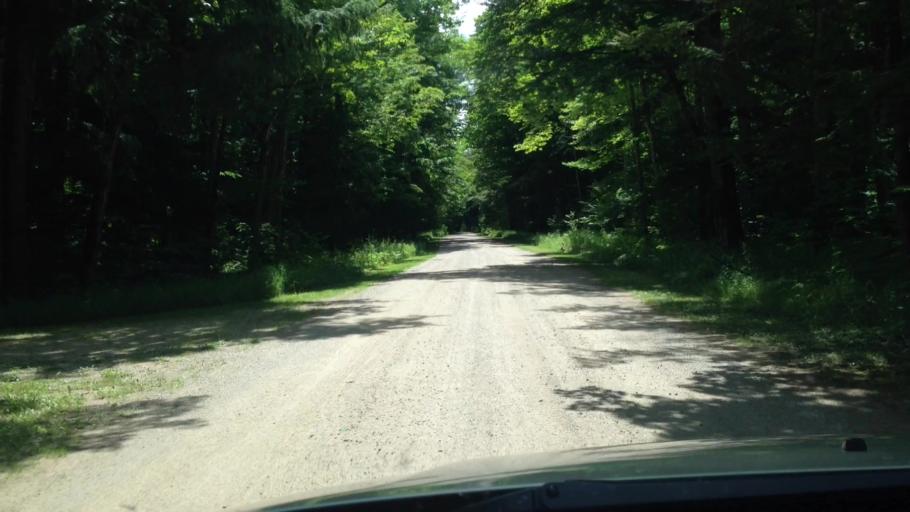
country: US
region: Michigan
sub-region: Menominee County
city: Menominee
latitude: 45.3976
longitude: -87.3640
